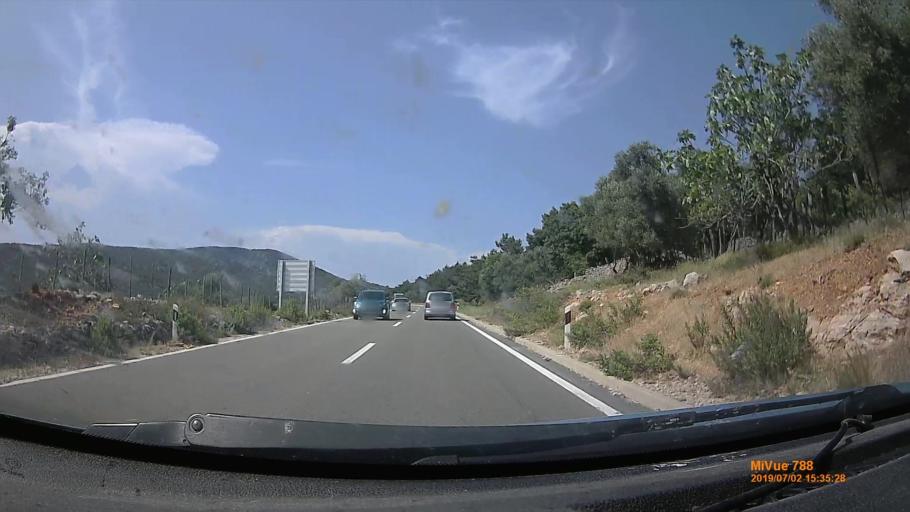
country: HR
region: Primorsko-Goranska
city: Cres
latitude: 44.9763
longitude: 14.4124
